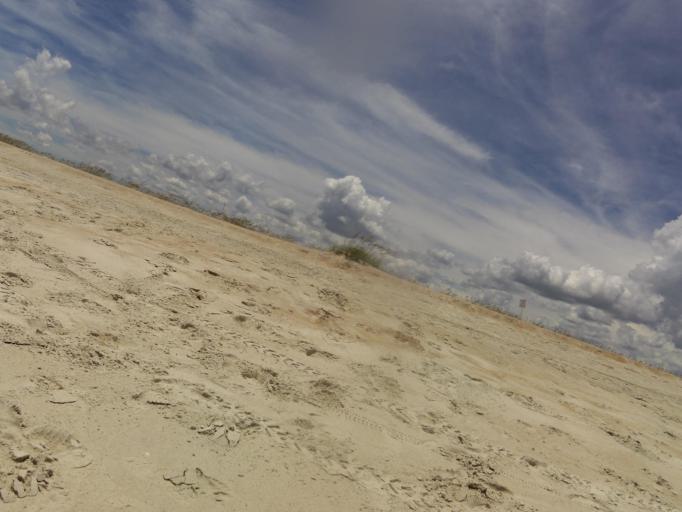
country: US
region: Florida
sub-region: Saint Johns County
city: Saint Augustine Beach
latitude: 29.8628
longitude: -81.2664
